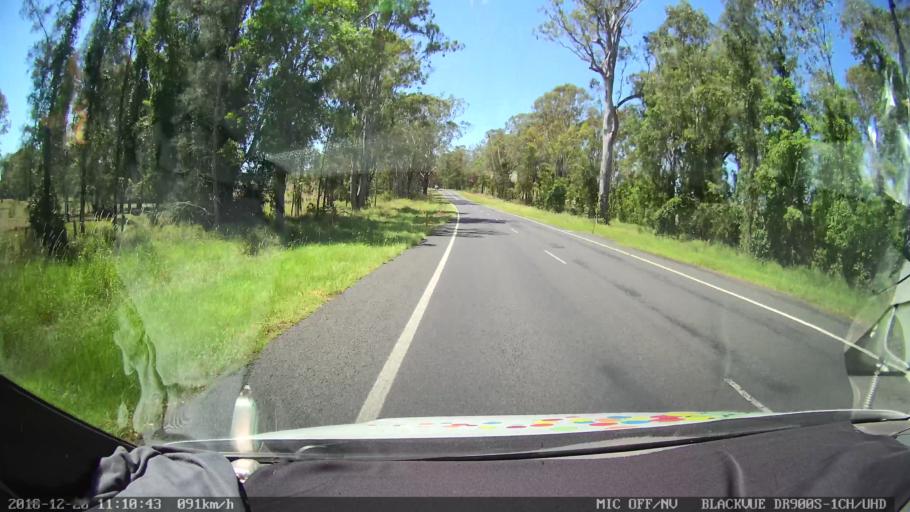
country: AU
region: New South Wales
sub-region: Richmond Valley
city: Casino
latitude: -28.9527
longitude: 153.0102
